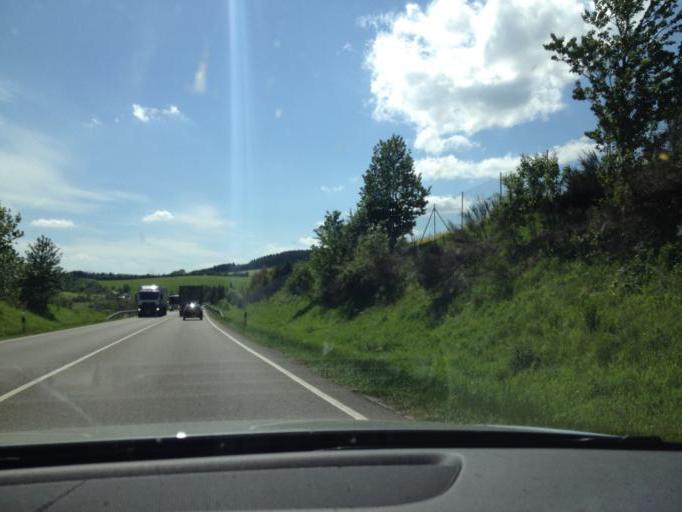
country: DE
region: Rheinland-Pfalz
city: Prum
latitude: 50.1891
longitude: 6.4253
